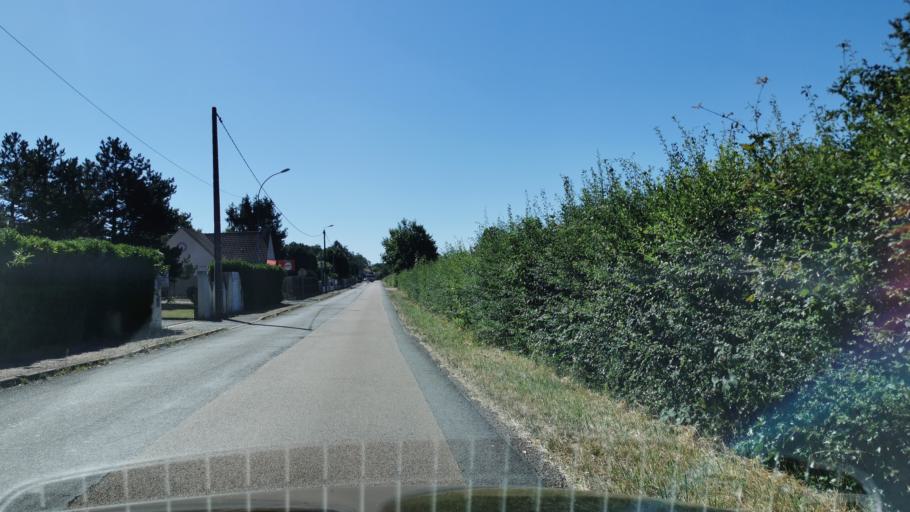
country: FR
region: Bourgogne
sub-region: Departement de Saone-et-Loire
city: Montchanin
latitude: 46.7531
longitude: 4.4906
